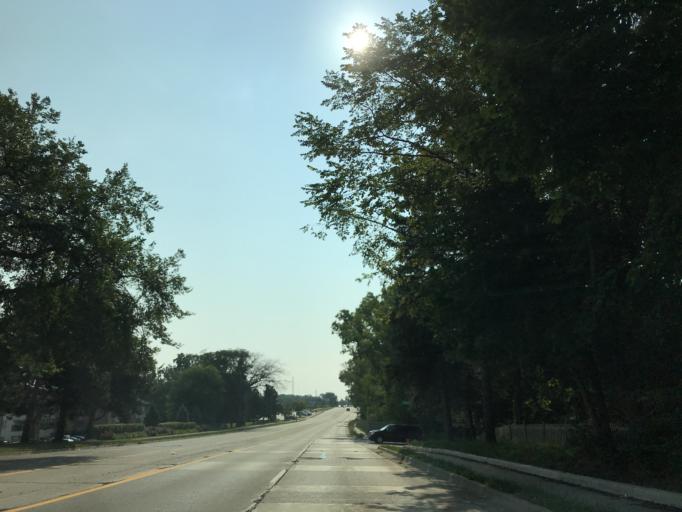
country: US
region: Michigan
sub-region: Washtenaw County
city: Ypsilanti
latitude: 42.2526
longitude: -83.6737
